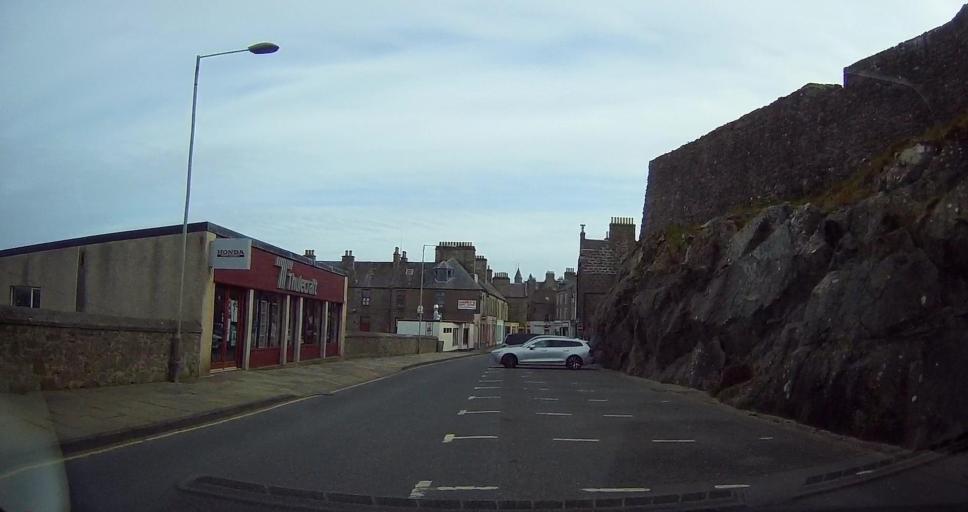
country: GB
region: Scotland
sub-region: Shetland Islands
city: Shetland
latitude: 60.1554
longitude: -1.1438
